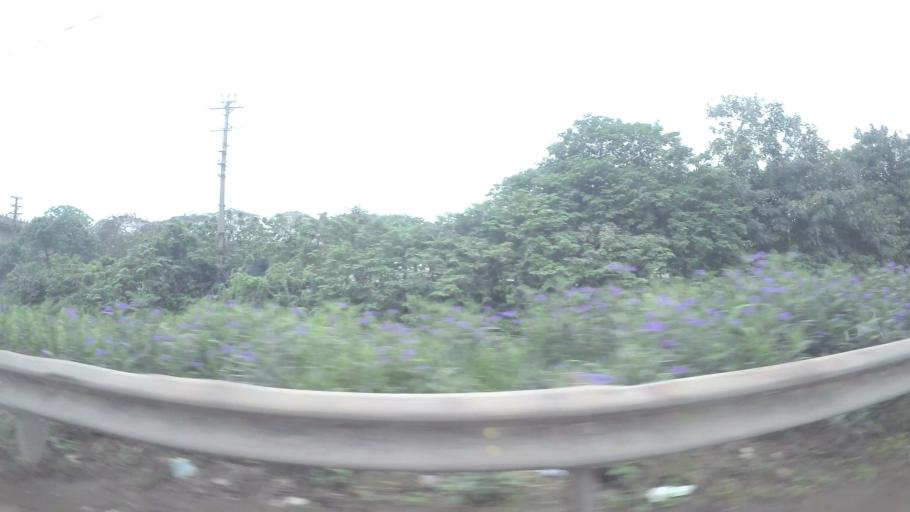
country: VN
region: Ha Noi
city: Trau Quy
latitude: 20.9866
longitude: 105.8949
